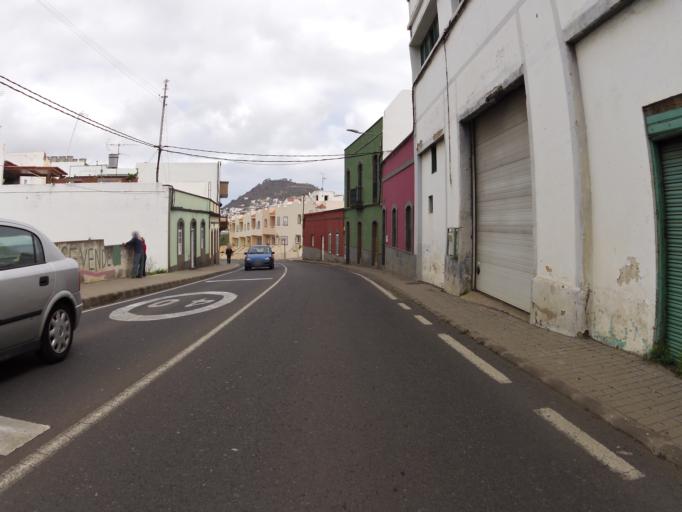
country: ES
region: Canary Islands
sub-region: Provincia de Las Palmas
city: Arucas
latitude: 28.1086
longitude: -15.5260
